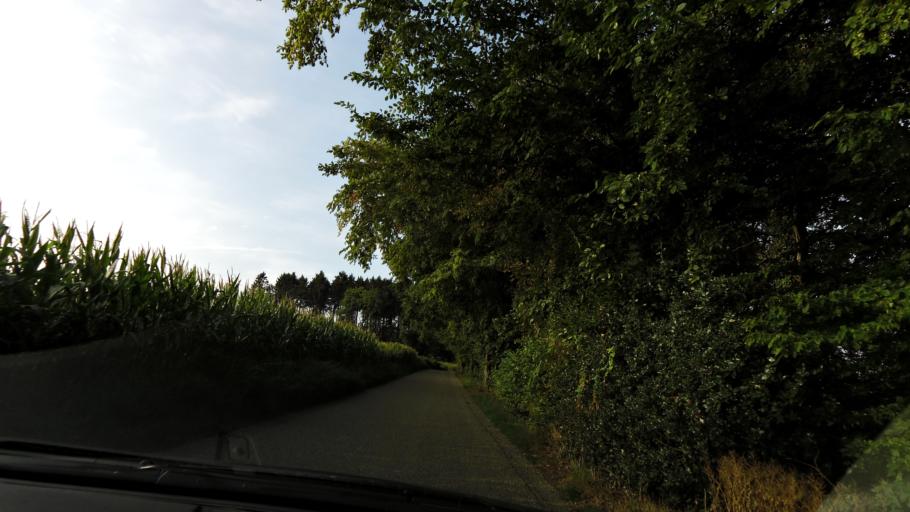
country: BE
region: Wallonia
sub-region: Province de Liege
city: Plombieres
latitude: 50.7804
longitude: 5.9660
